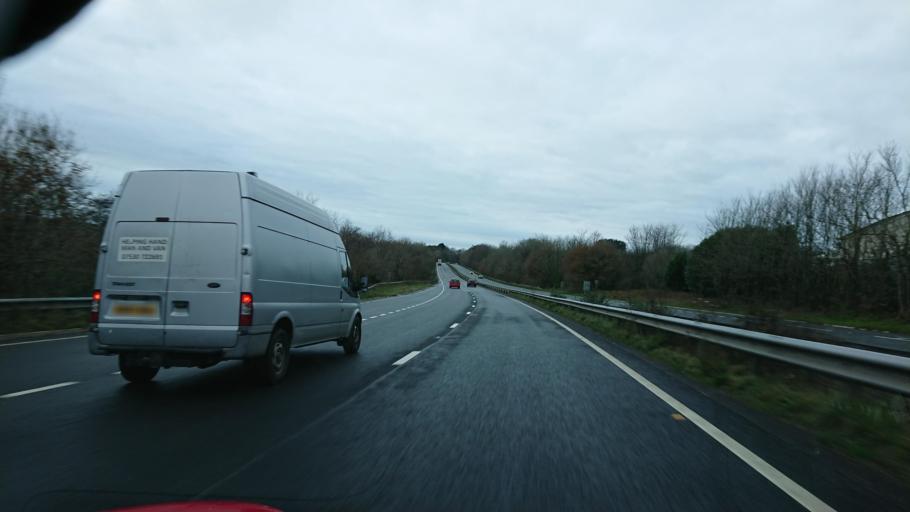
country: GB
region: England
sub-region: Cornwall
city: Liskeard
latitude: 50.4506
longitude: -4.4576
